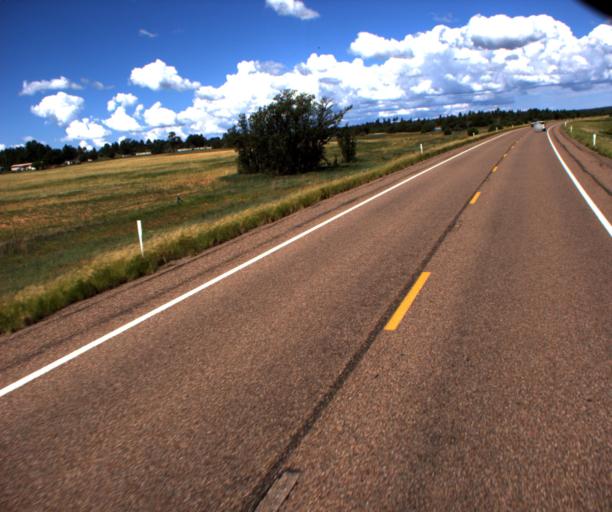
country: US
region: Arizona
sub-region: Navajo County
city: Linden
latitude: 34.3497
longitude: -110.3084
